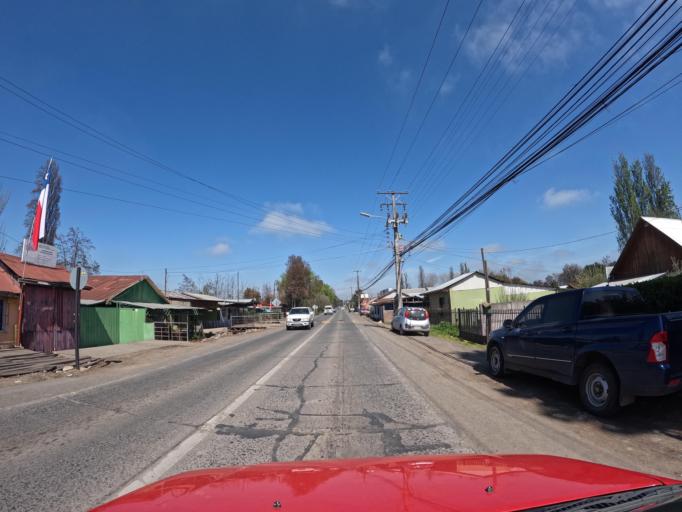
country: CL
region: Maule
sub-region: Provincia de Curico
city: Molina
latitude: -35.0799
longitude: -71.2617
